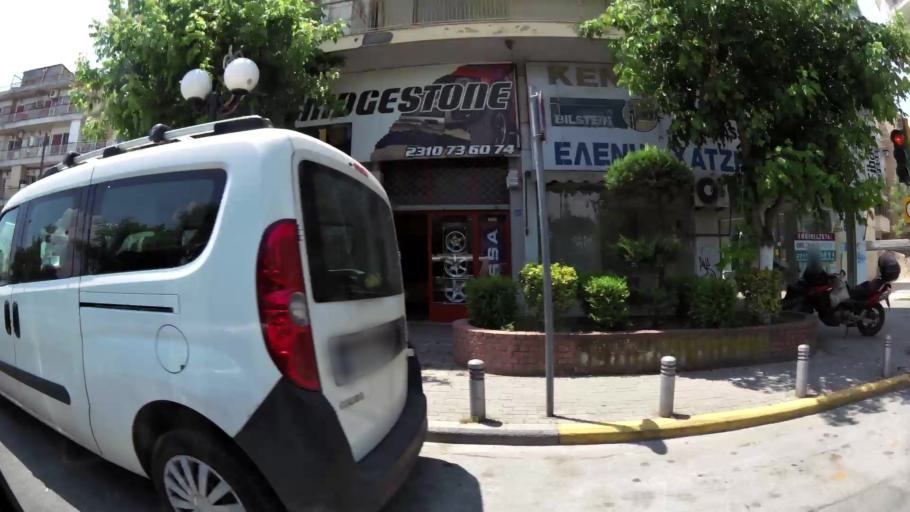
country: GR
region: Central Macedonia
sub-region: Nomos Thessalonikis
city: Ampelokipoi
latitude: 40.6577
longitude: 22.9141
